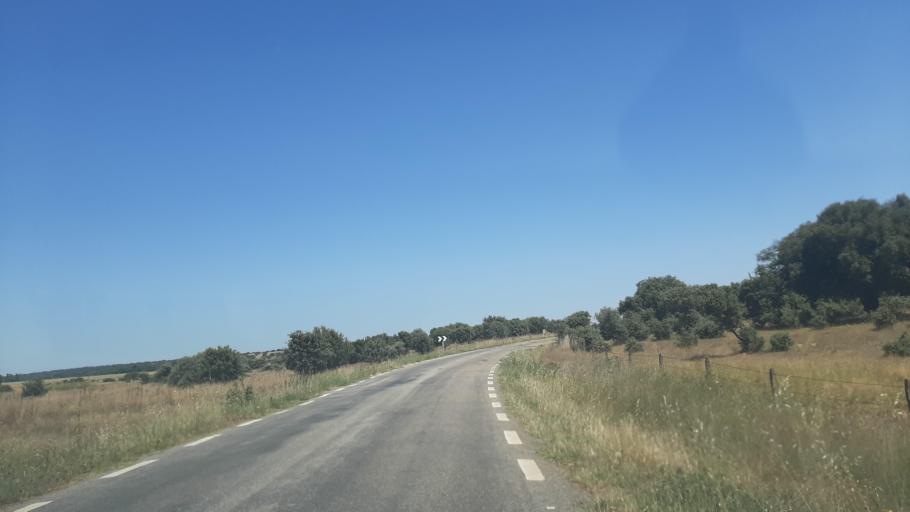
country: ES
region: Castille and Leon
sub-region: Provincia de Salamanca
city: Cabrillas
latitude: 40.7300
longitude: -6.1773
